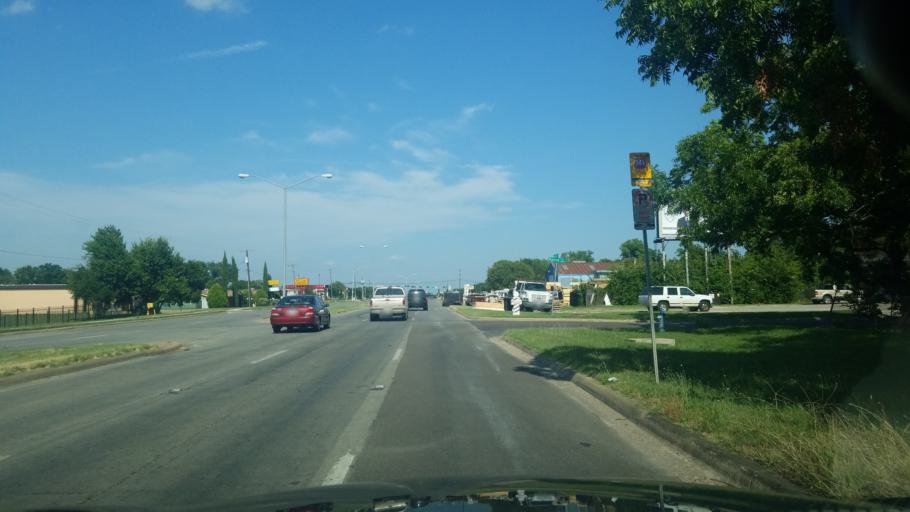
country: US
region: Texas
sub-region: Dallas County
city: Dallas
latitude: 32.7167
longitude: -96.7806
